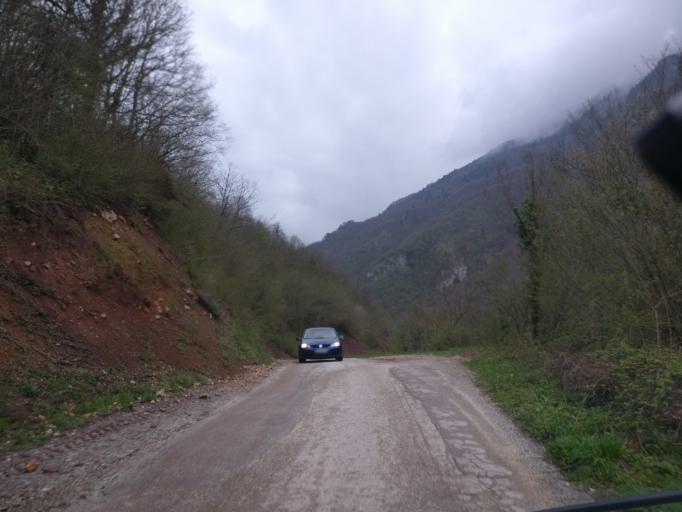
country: BA
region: Republika Srpska
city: Foca
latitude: 43.3569
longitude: 18.8166
